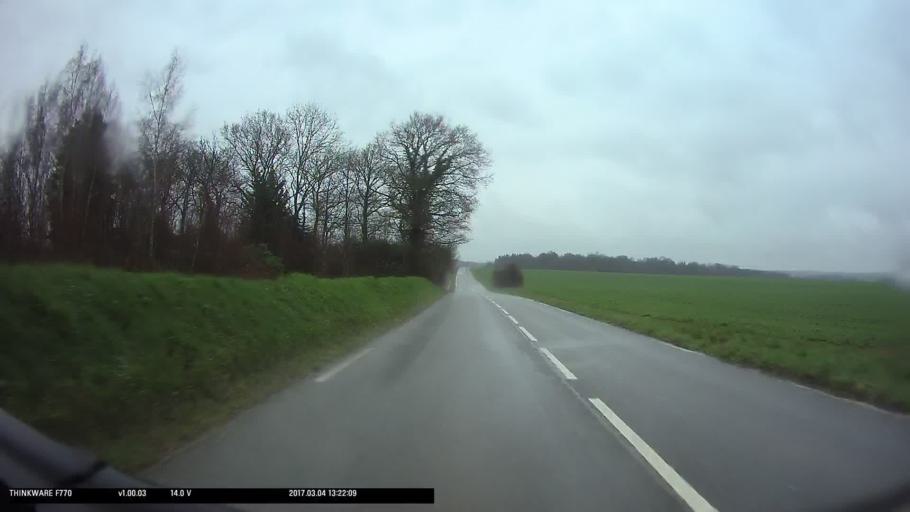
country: FR
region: Ile-de-France
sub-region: Departement du Val-d'Oise
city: Marines
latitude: 49.1215
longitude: 1.9817
